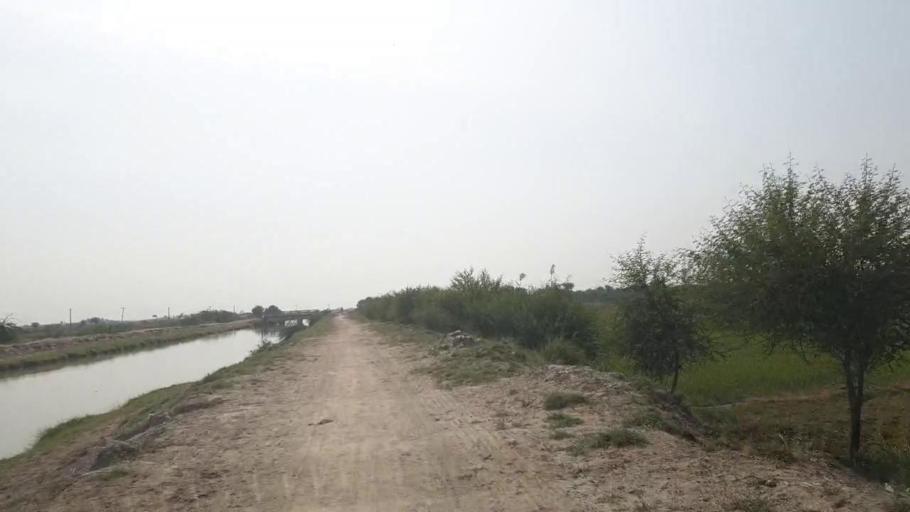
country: PK
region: Sindh
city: Badin
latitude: 24.5552
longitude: 68.8495
